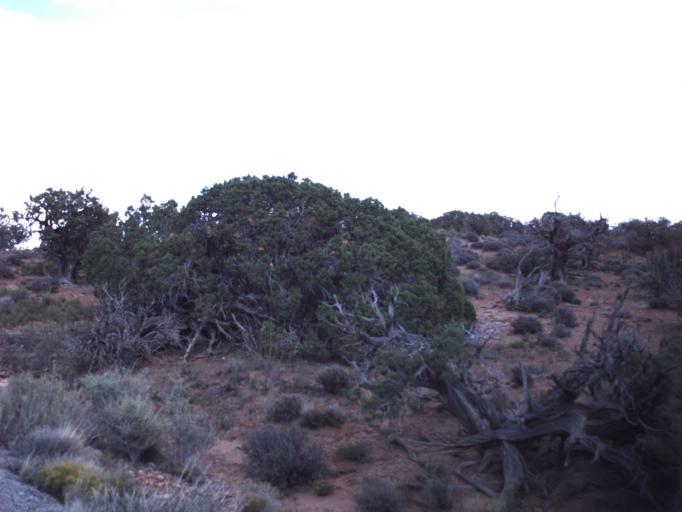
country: US
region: Utah
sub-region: Grand County
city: Moab
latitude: 38.4786
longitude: -109.7396
